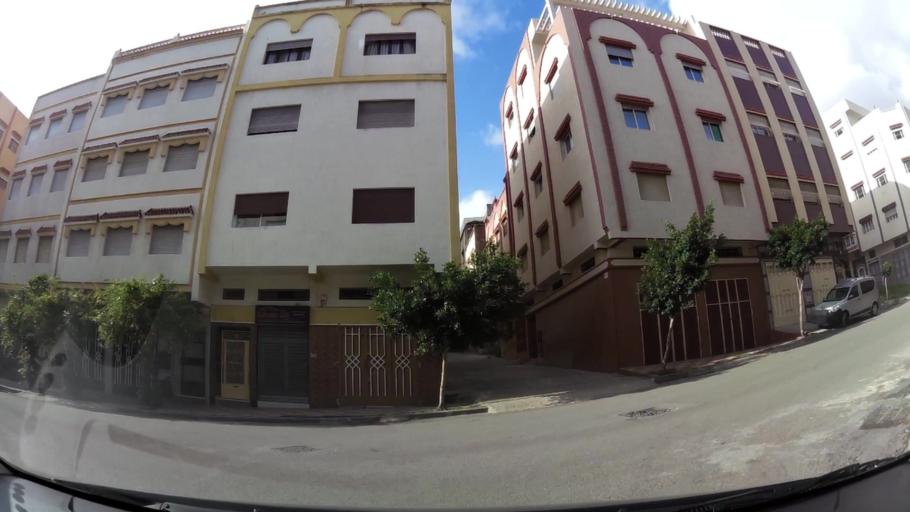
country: MA
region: Tanger-Tetouan
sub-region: Tanger-Assilah
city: Tangier
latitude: 35.7643
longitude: -5.8331
